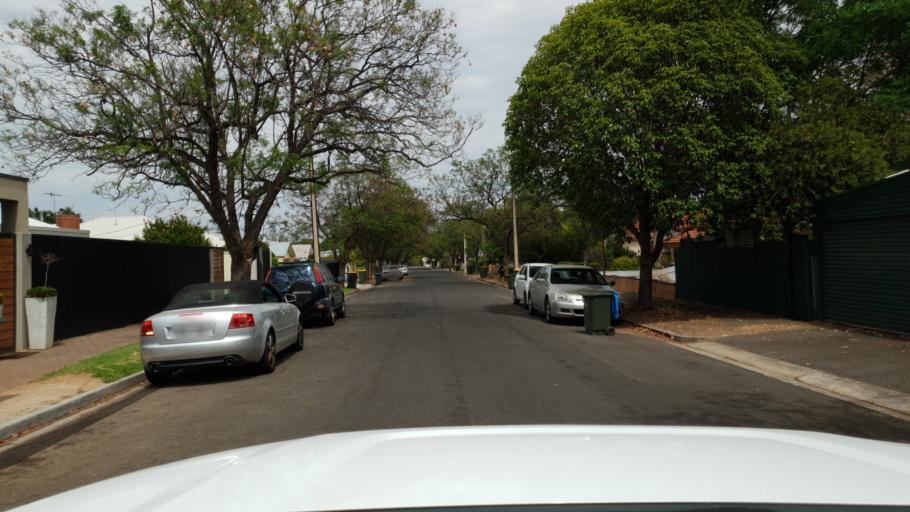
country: AU
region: South Australia
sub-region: Mitcham
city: Clarence Gardens
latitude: -34.9691
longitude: 138.5795
